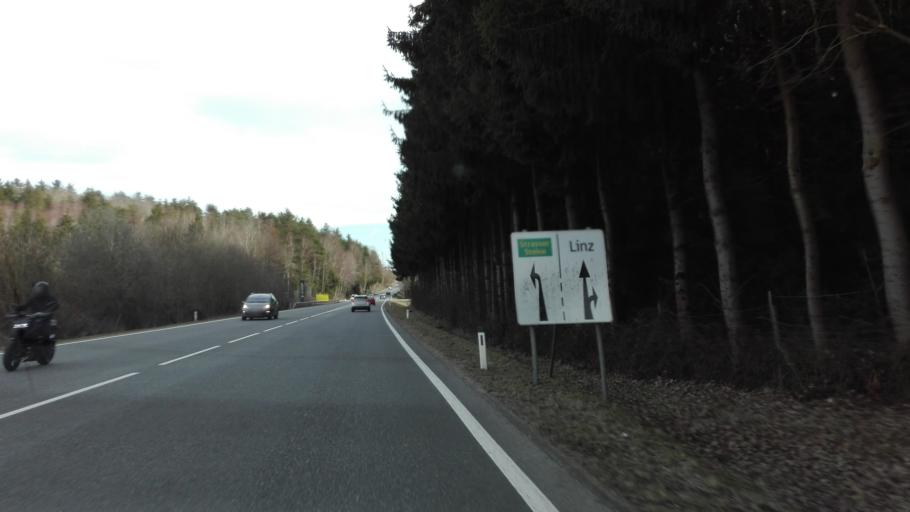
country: AT
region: Upper Austria
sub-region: Politischer Bezirk Urfahr-Umgebung
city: Herzogsdorf
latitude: 48.4246
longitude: 14.0537
